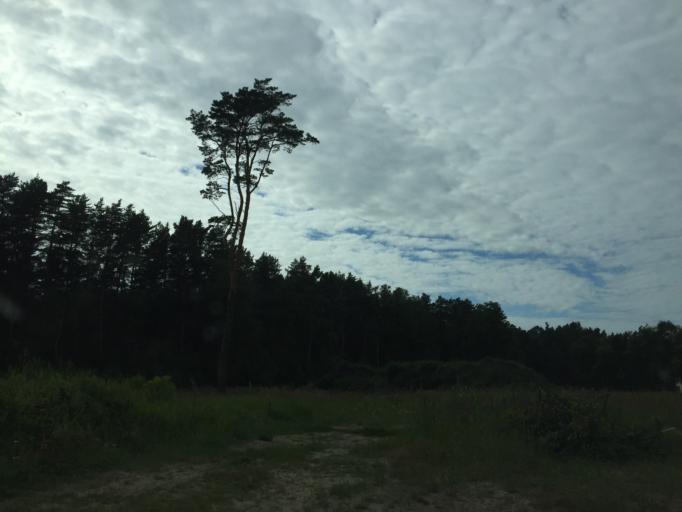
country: LV
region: Riga
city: Jaunciems
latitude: 57.1069
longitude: 24.1941
